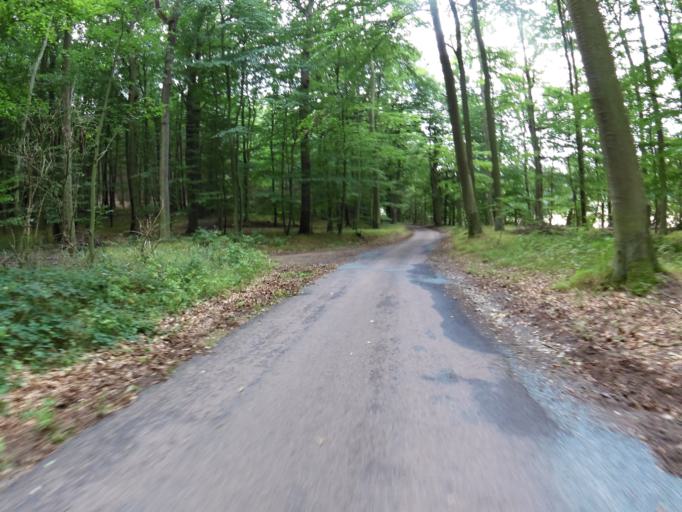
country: DE
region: Mecklenburg-Vorpommern
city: Seebad Heringsdorf
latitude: 53.8957
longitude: 14.1640
